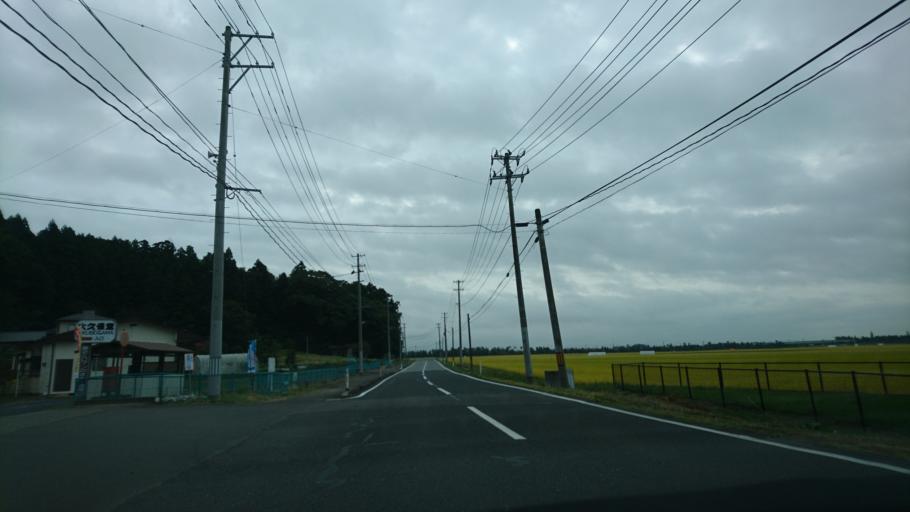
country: JP
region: Iwate
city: Ichinoseki
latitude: 38.8065
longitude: 141.0867
